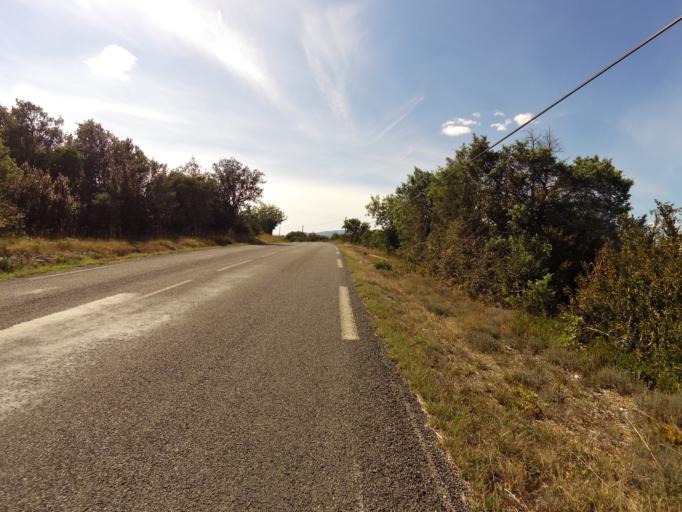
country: FR
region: Languedoc-Roussillon
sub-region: Departement du Gard
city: Lezan
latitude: 43.9595
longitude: 4.0415
